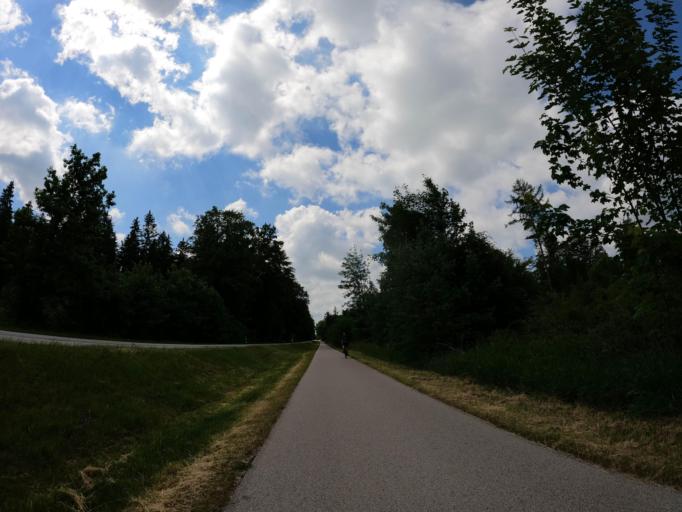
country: DE
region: Bavaria
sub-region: Upper Bavaria
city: Oberhaching
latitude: 48.0035
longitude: 11.5793
